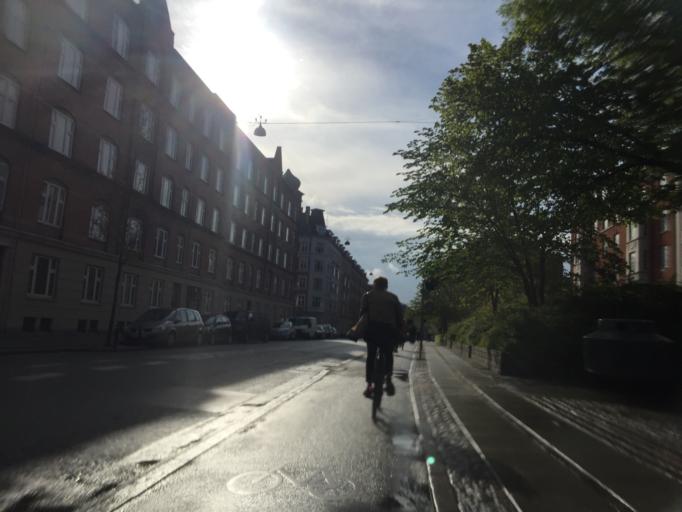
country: DK
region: Capital Region
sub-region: Frederiksberg Kommune
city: Frederiksberg
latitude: 55.6837
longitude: 12.5275
